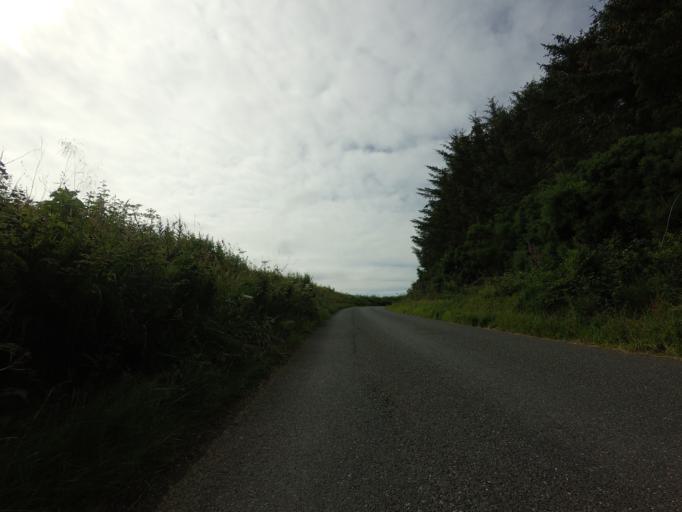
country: GB
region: Scotland
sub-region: Aberdeenshire
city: Turriff
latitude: 57.5335
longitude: -2.4022
